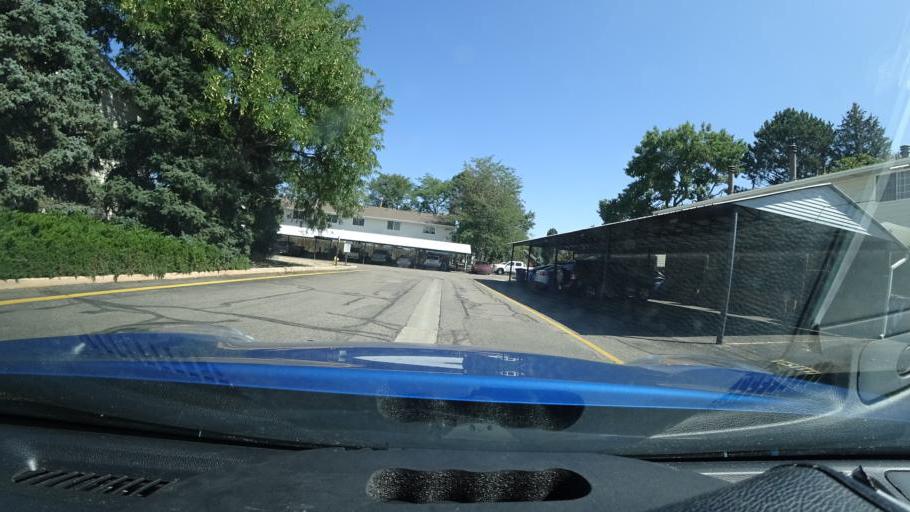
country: US
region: Colorado
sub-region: Adams County
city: Aurora
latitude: 39.6834
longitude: -104.8239
